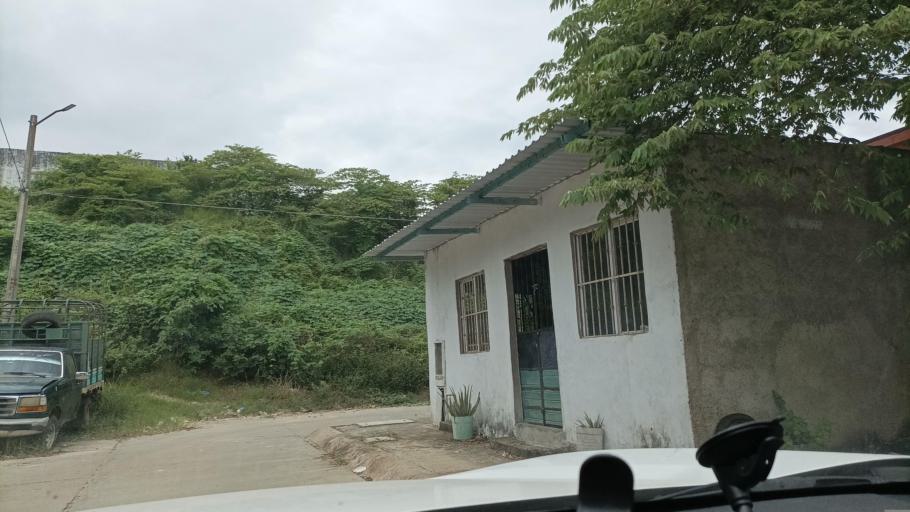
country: MX
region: Veracruz
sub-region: Soconusco
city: Fraccionamiento Santa Cruz
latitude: 17.9714
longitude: -94.8984
